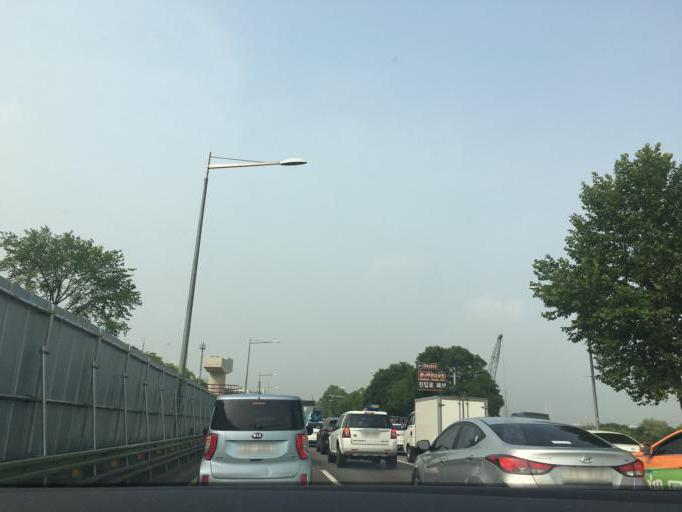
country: KR
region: Gyeonggi-do
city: Guri-si
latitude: 37.5277
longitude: 127.1070
